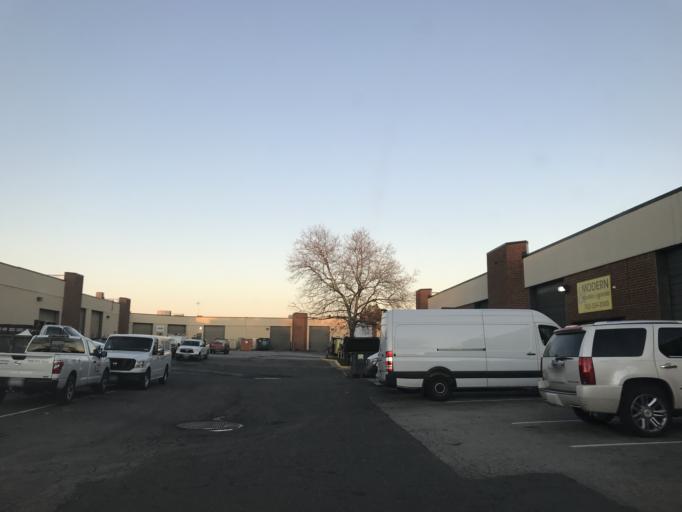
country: US
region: Virginia
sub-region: Fairfax County
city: Springfield
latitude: 38.7956
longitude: -77.1660
